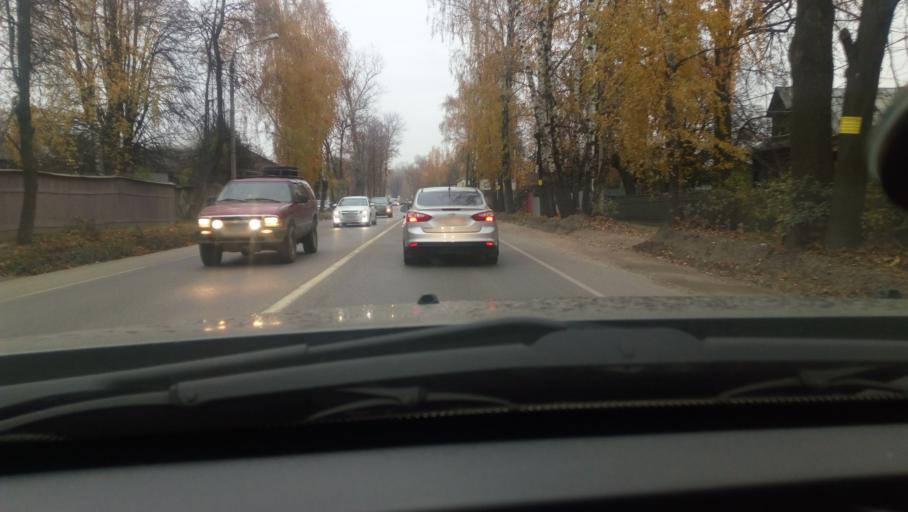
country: RU
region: Moskovskaya
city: Saltykovka
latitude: 55.7523
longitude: 37.9136
